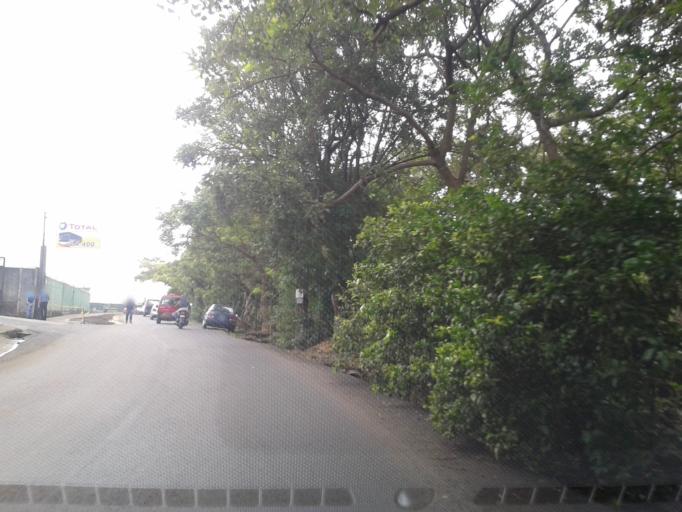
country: CR
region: Heredia
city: San Pablo
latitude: 9.9854
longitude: -84.1071
